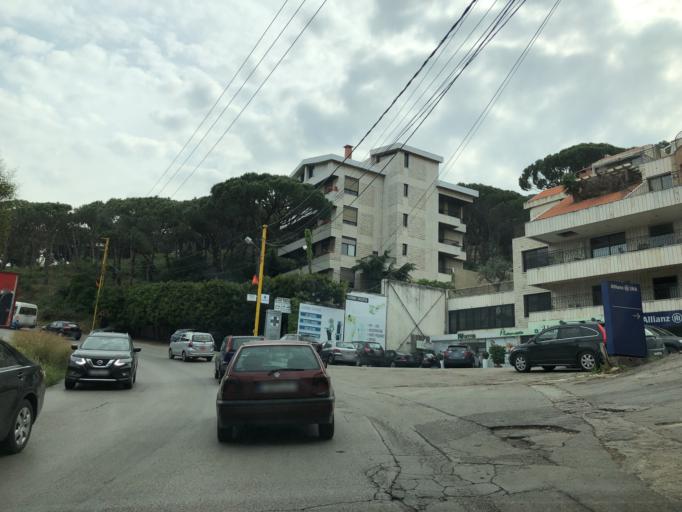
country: LB
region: Mont-Liban
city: Jdaidet el Matn
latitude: 33.8555
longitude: 35.5872
